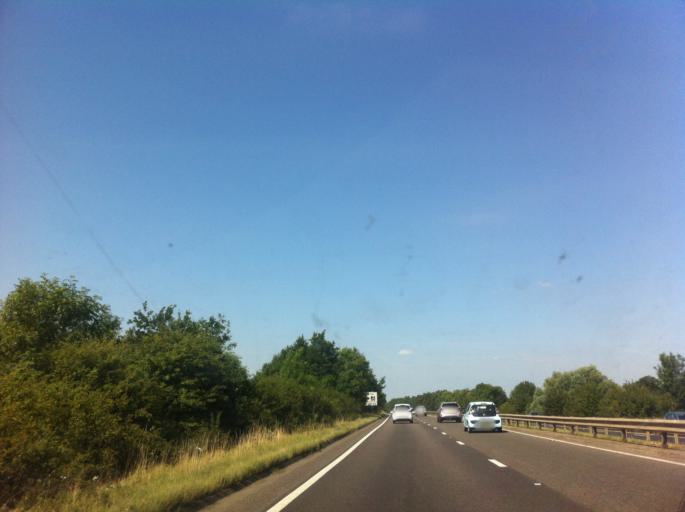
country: GB
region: England
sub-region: Northamptonshire
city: Earls Barton
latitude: 52.2553
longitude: -0.7732
